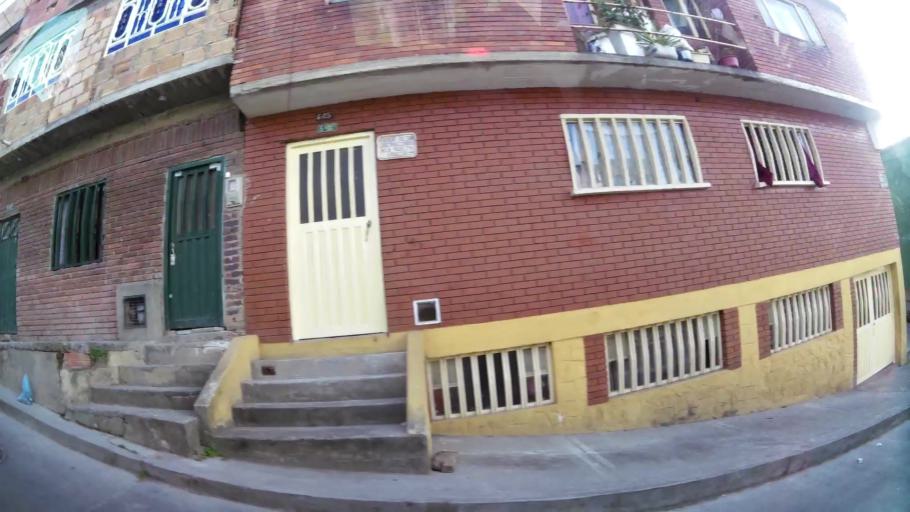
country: CO
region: Bogota D.C.
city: Bogota
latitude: 4.5439
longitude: -74.0936
